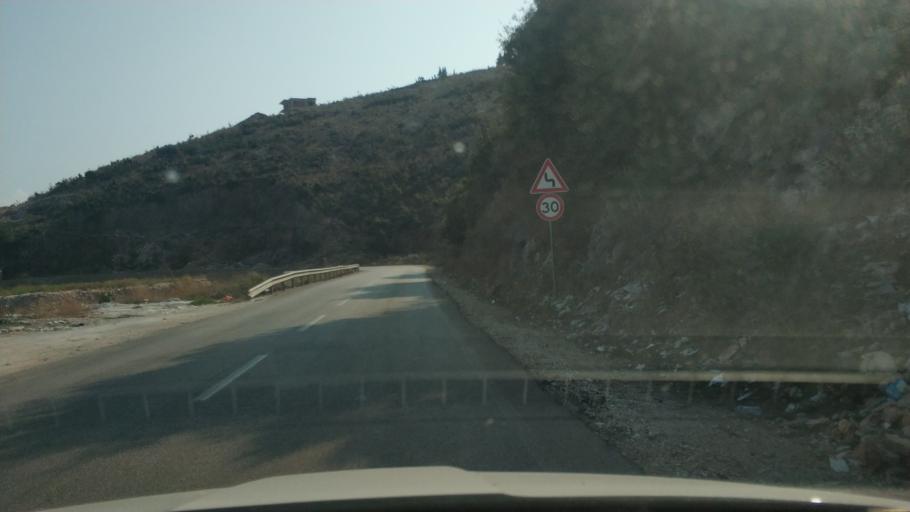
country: AL
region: Vlore
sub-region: Rrethi i Sarandes
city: Sarande
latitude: 39.8558
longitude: 20.0352
